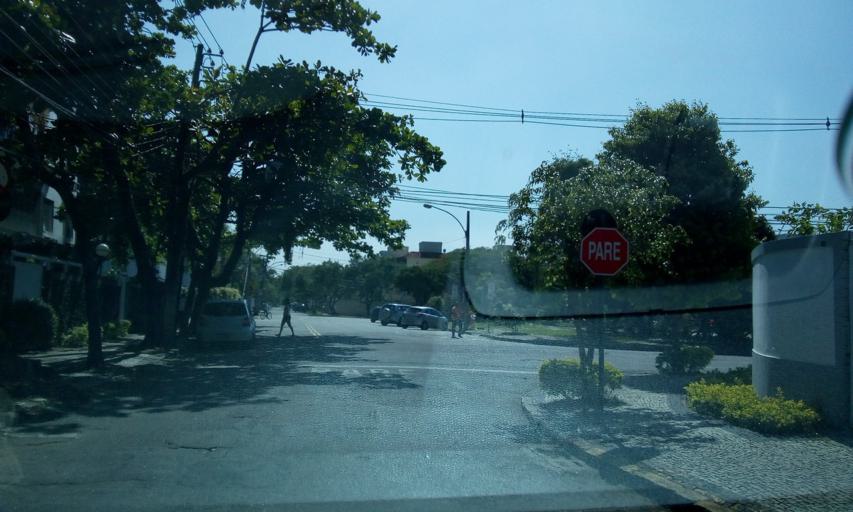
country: BR
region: Rio de Janeiro
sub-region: Nilopolis
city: Nilopolis
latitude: -23.0143
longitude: -43.4589
